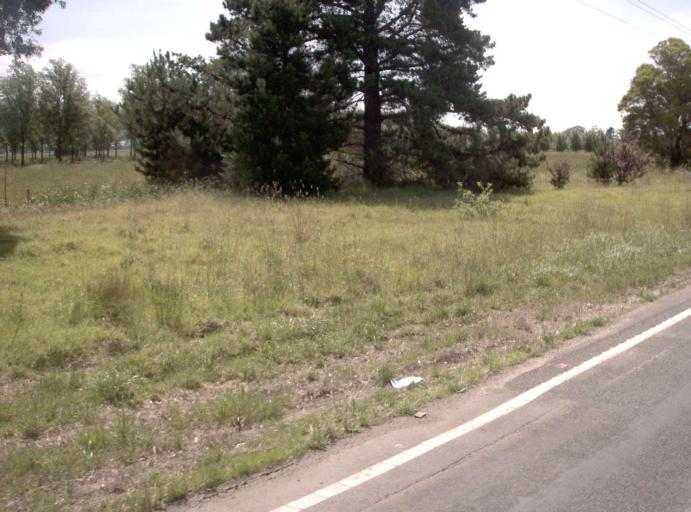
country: AU
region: Victoria
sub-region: Wellington
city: Sale
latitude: -38.0518
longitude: 147.0665
